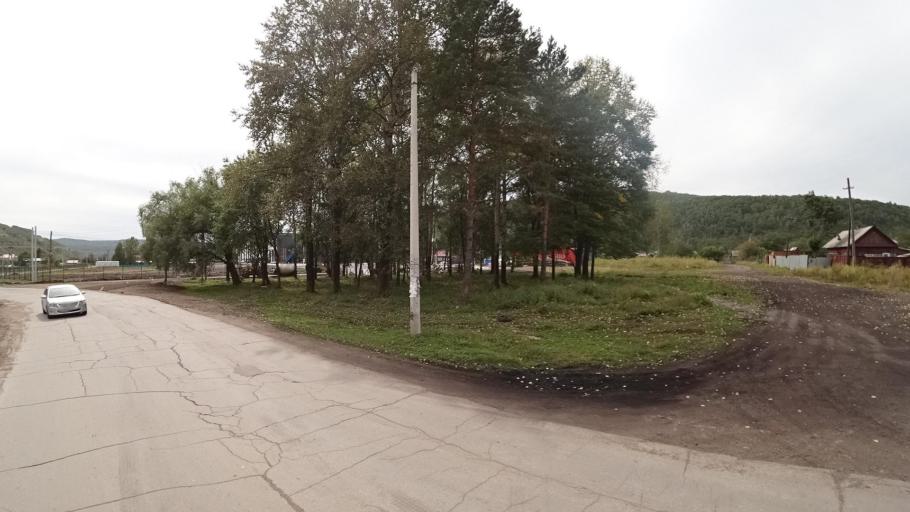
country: RU
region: Jewish Autonomous Oblast
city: Khingansk
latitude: 49.0043
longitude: 131.0539
